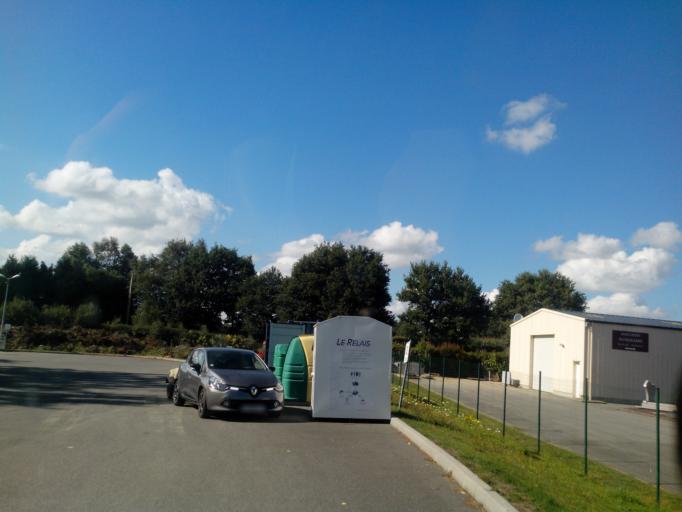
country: FR
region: Brittany
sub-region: Departement des Cotes-d'Armor
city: Merdrignac
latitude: 48.1924
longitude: -2.4010
